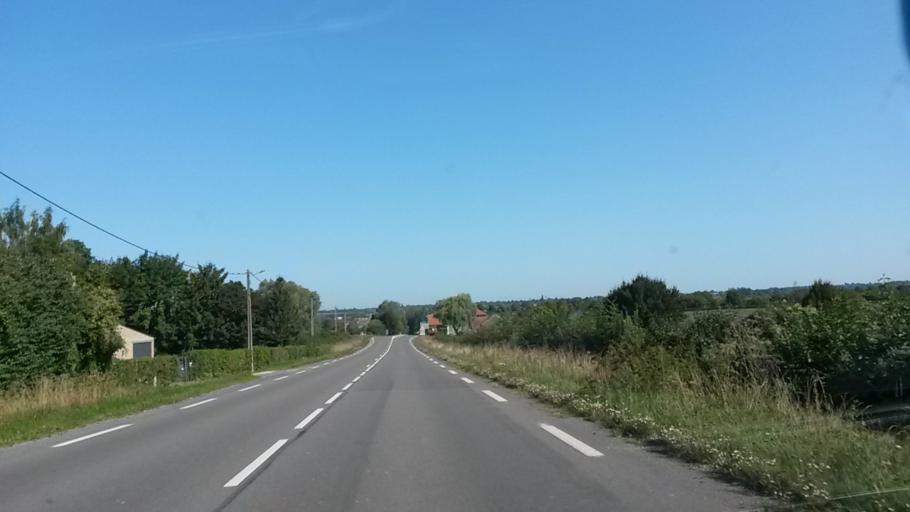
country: FR
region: Picardie
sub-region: Departement de l'Aisne
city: La Flamengrie
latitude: 50.0467
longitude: 3.9271
